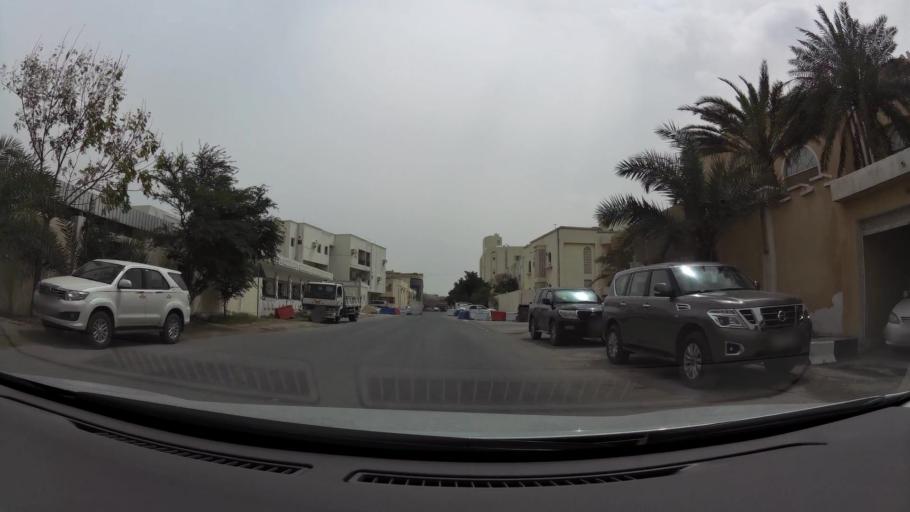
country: QA
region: Baladiyat ad Dawhah
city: Doha
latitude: 25.2527
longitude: 51.5509
